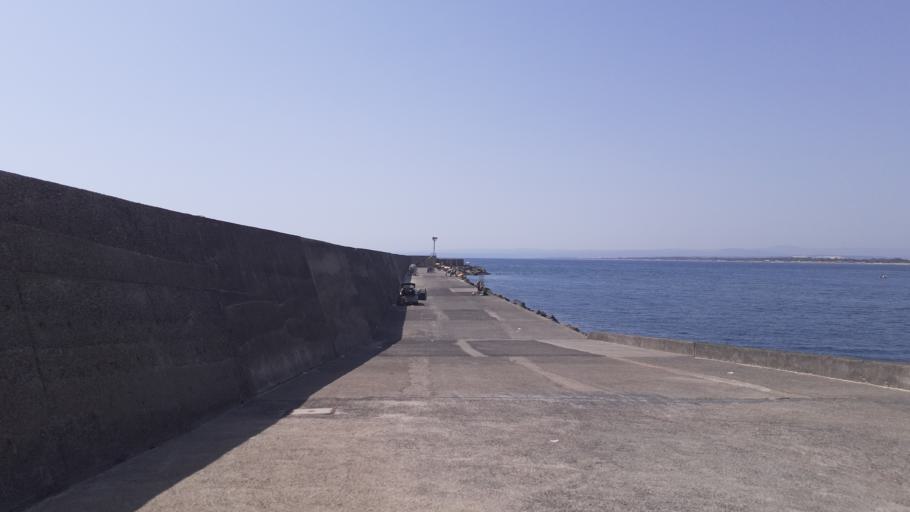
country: IT
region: Sicily
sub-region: Catania
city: Catania
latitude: 37.4867
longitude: 15.0993
